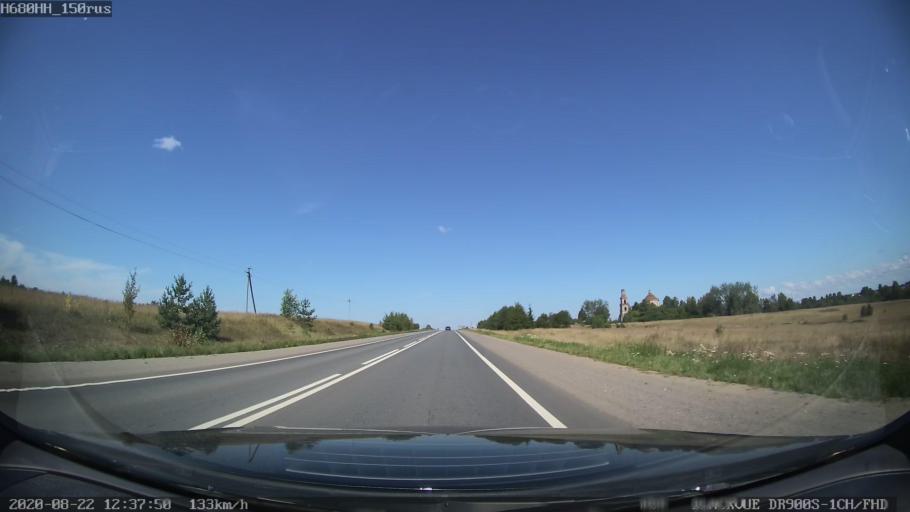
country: RU
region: Tverskaya
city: Rameshki
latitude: 57.3034
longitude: 36.0888
